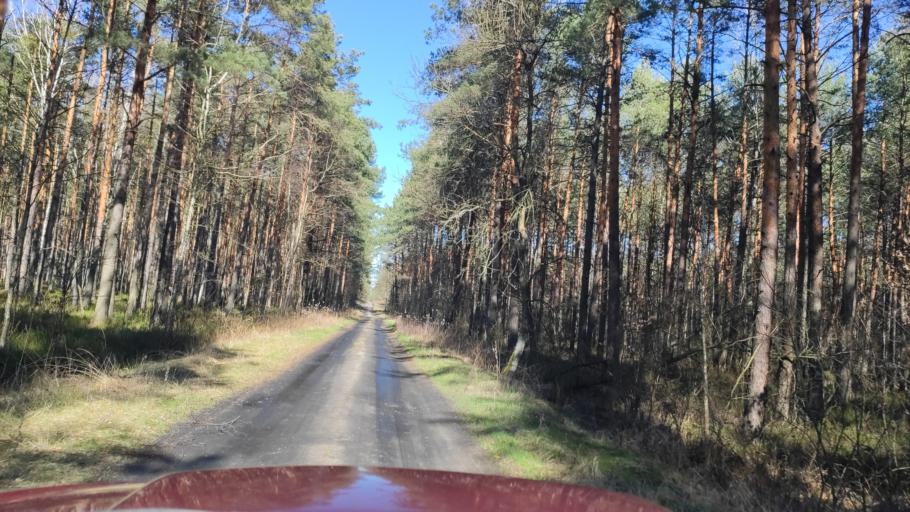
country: PL
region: Masovian Voivodeship
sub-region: Powiat zwolenski
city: Zwolen
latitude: 51.4100
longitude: 21.5570
